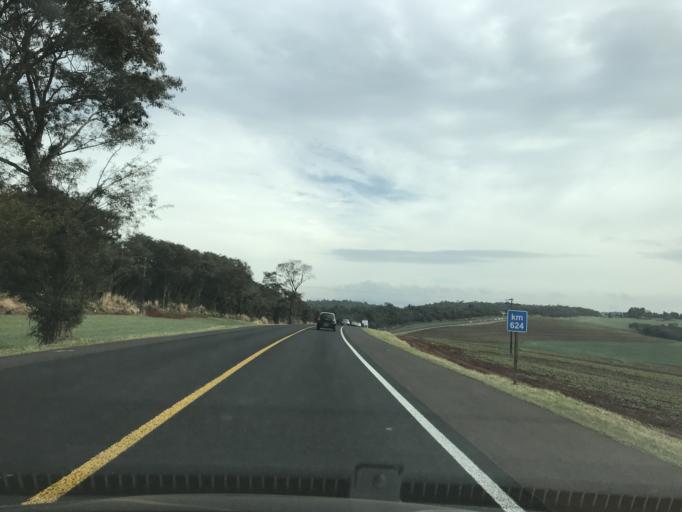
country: BR
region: Parana
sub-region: Matelandia
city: Matelandia
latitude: -25.1042
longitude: -53.7404
